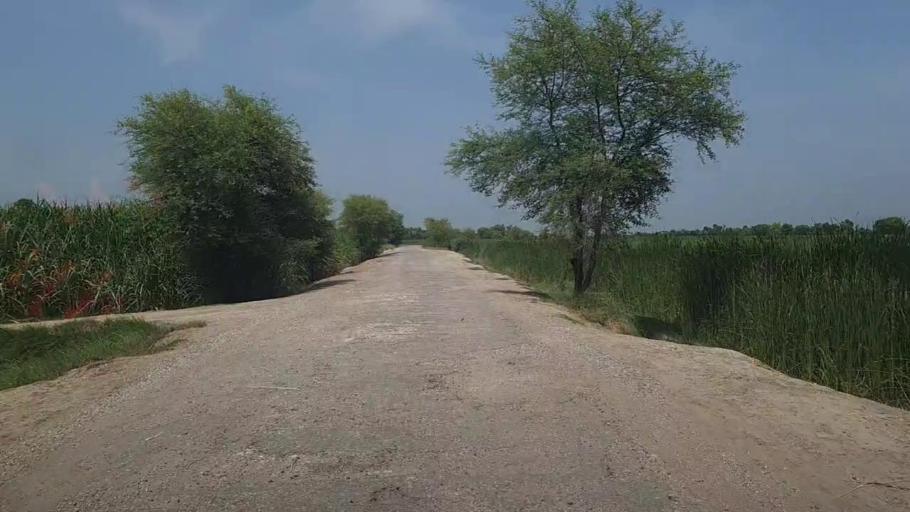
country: PK
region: Sindh
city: Ubauro
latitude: 28.1627
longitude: 69.8282
